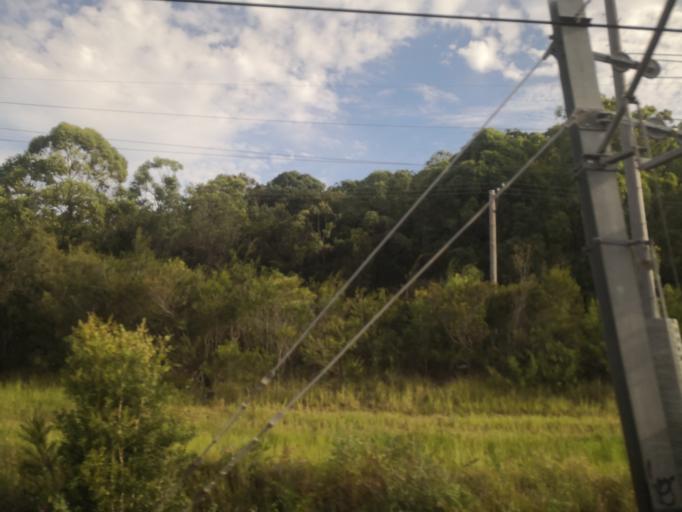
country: AU
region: New South Wales
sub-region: Gosford Shire
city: Blackwall
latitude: -33.4975
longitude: 151.3016
